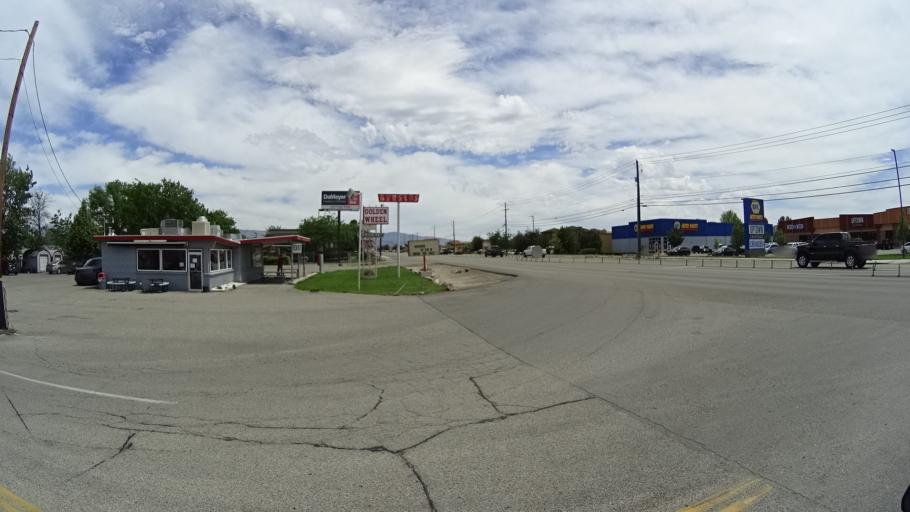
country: US
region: Idaho
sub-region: Ada County
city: Meridian
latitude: 43.6196
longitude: -116.3206
